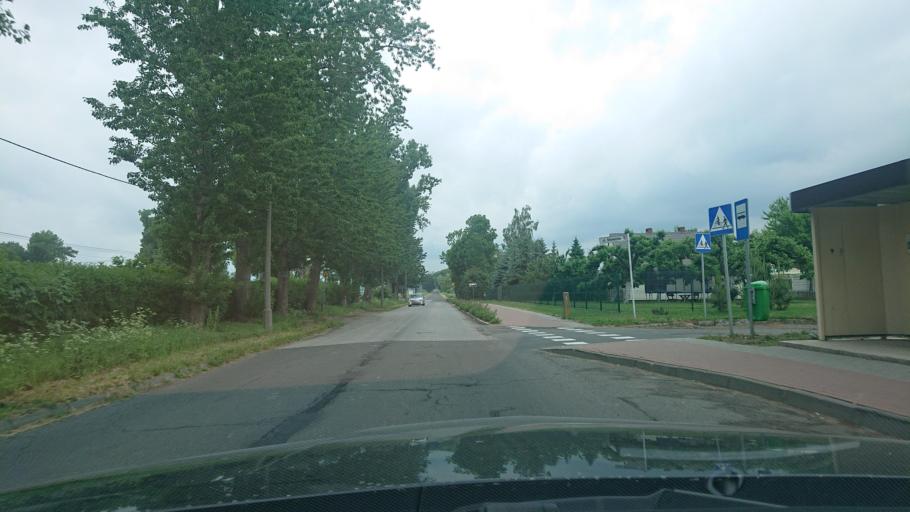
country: PL
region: Greater Poland Voivodeship
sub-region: Powiat gnieznienski
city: Gniezno
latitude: 52.4527
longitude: 17.5768
